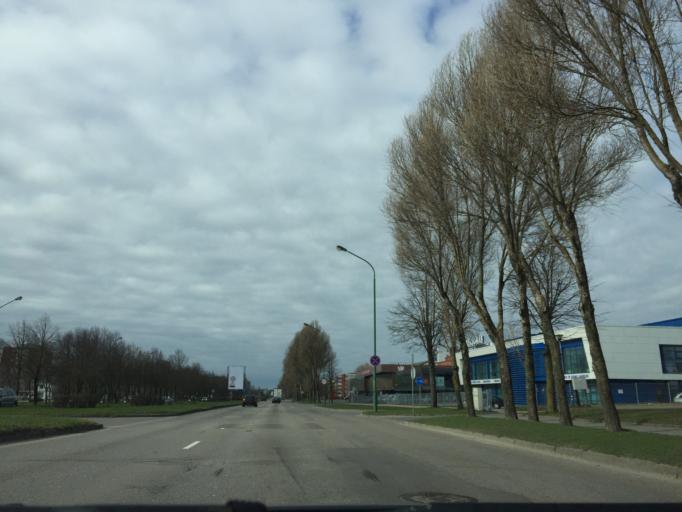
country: LT
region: Klaipedos apskritis
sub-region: Klaipeda
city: Klaipeda
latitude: 55.6900
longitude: 21.1701
